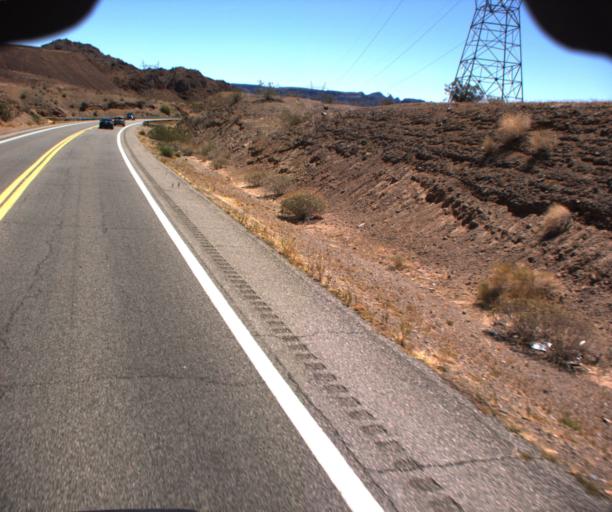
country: US
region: Arizona
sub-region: La Paz County
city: Cienega Springs
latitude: 34.3390
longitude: -114.1422
